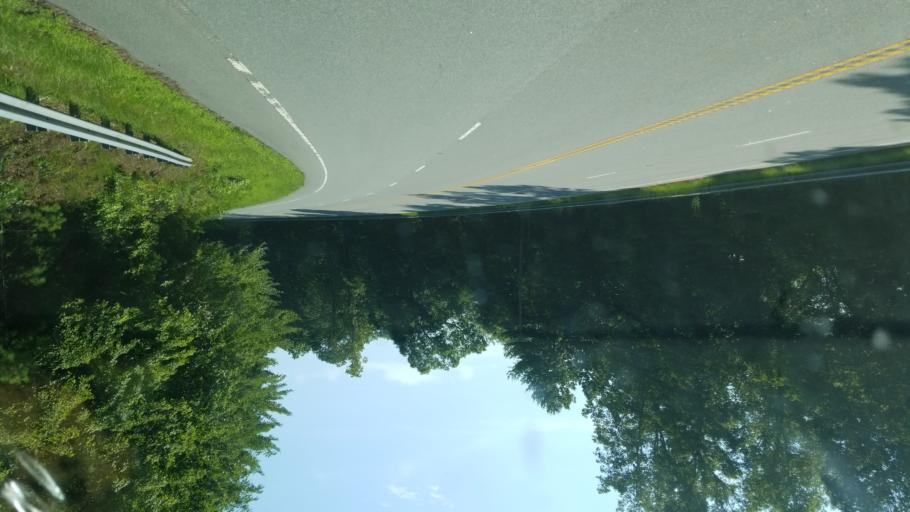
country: US
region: North Carolina
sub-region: Burke County
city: Glen Alpine
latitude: 35.8927
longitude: -81.8032
